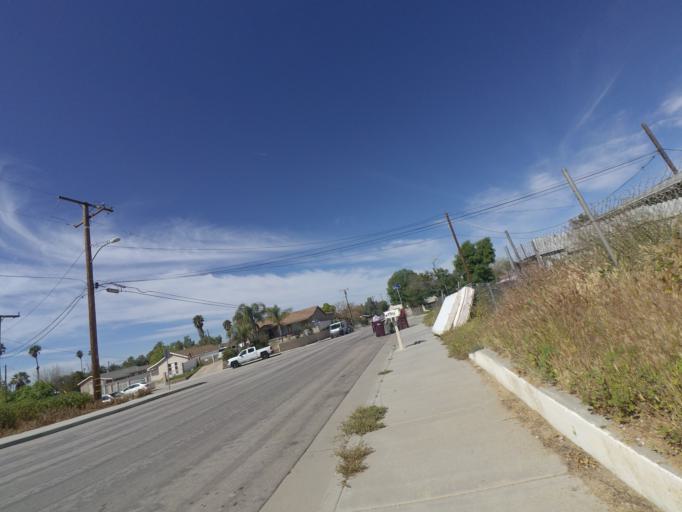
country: US
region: California
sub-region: Riverside County
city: March Air Force Base
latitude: 33.9190
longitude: -117.2739
